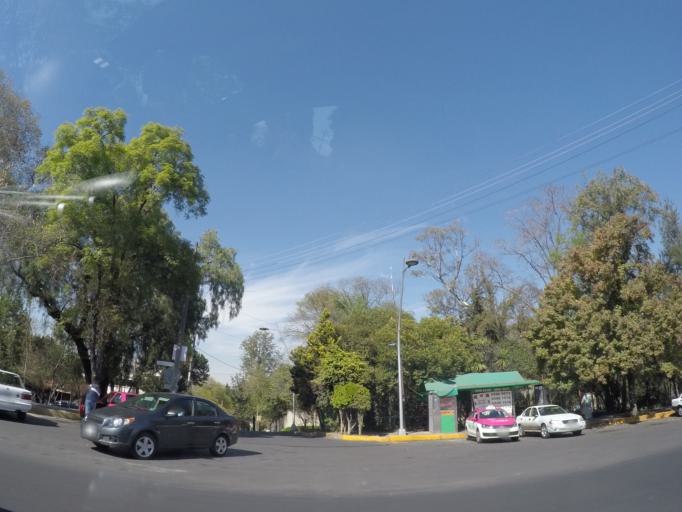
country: MX
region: Mexico City
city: Polanco
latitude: 19.4067
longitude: -99.2262
